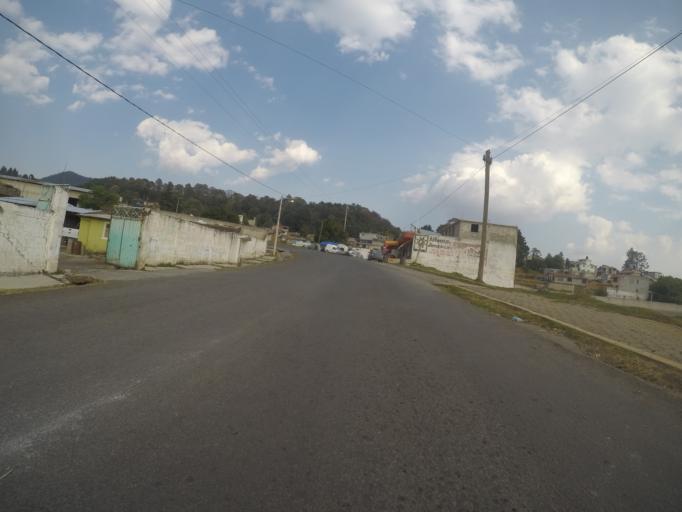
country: MX
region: Mexico
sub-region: Xalatlaco
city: El Aguila (La Mesa)
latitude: 19.1570
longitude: -99.3993
